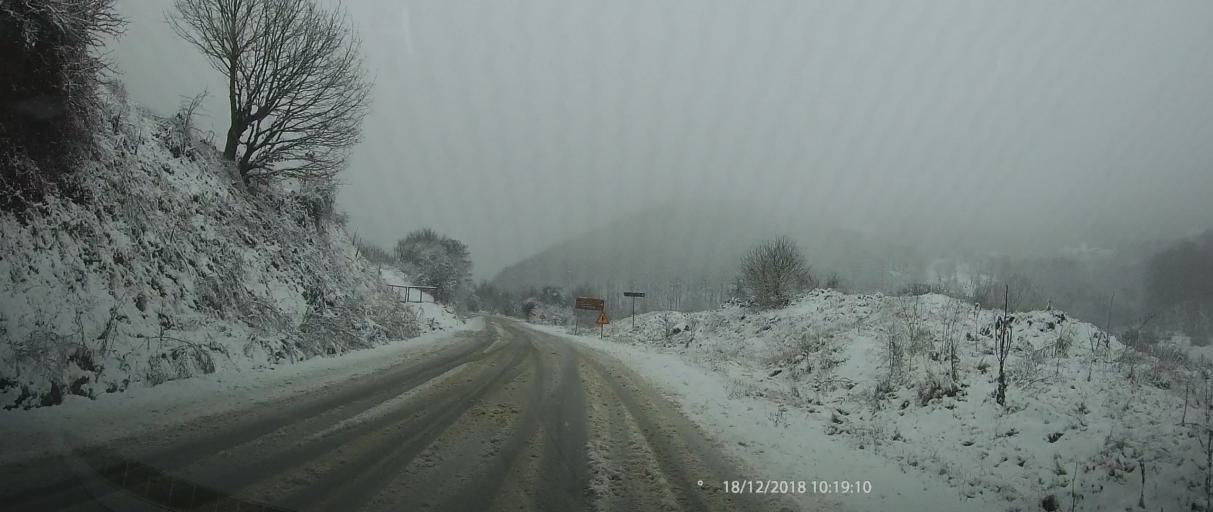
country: GR
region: Thessaly
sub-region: Nomos Larisis
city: Livadi
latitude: 40.1370
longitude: 22.2214
